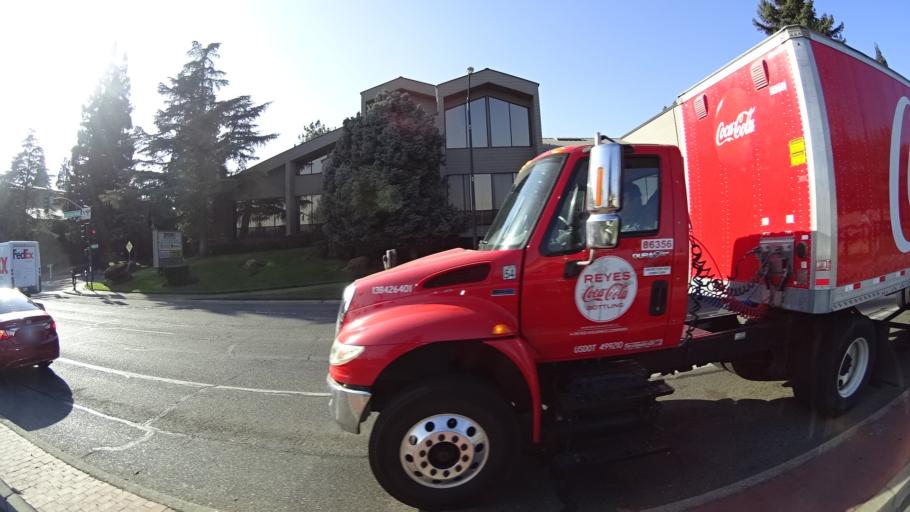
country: US
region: California
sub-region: Sacramento County
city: Citrus Heights
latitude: 38.6925
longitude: -121.2716
